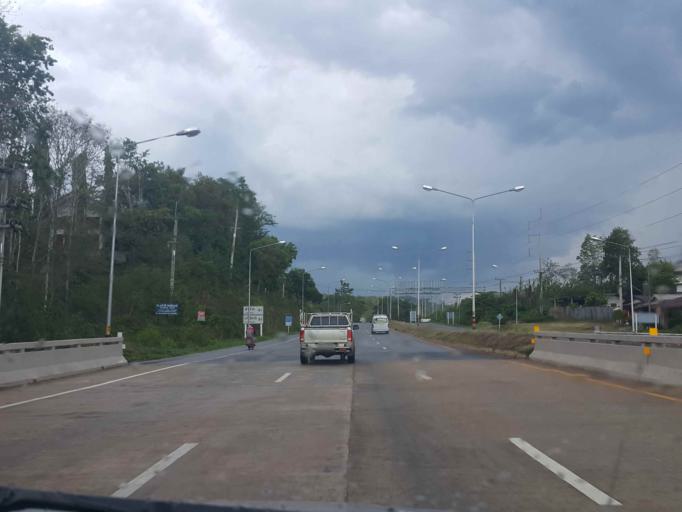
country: TH
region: Phrae
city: Den Chai
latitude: 17.9686
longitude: 100.0638
